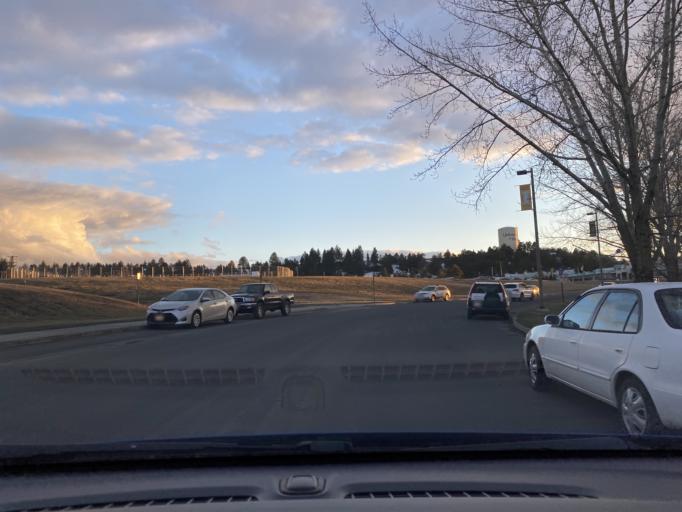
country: US
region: Idaho
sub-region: Latah County
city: Moscow
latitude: 46.7295
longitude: -117.0216
